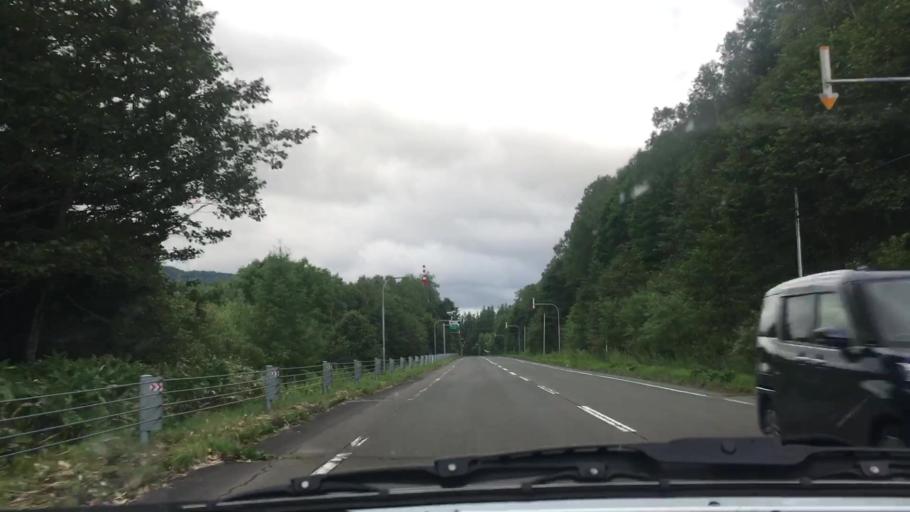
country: JP
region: Hokkaido
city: Shimo-furano
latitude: 43.0587
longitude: 142.6682
